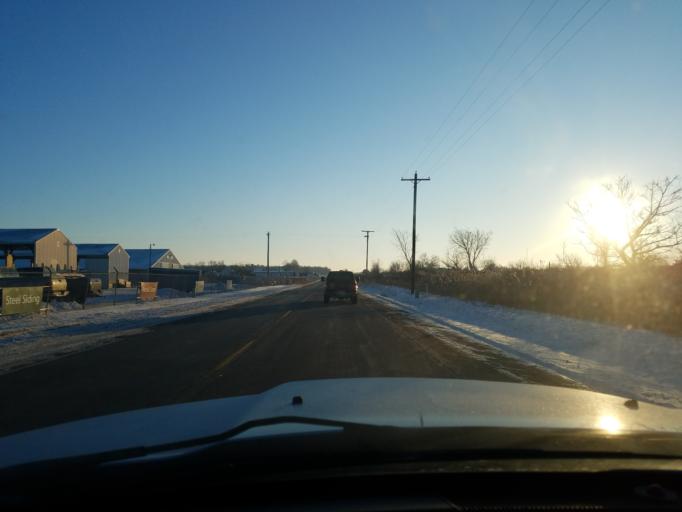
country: US
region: Indiana
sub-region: Marshall County
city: Bremen
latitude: 41.4467
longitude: -86.0750
